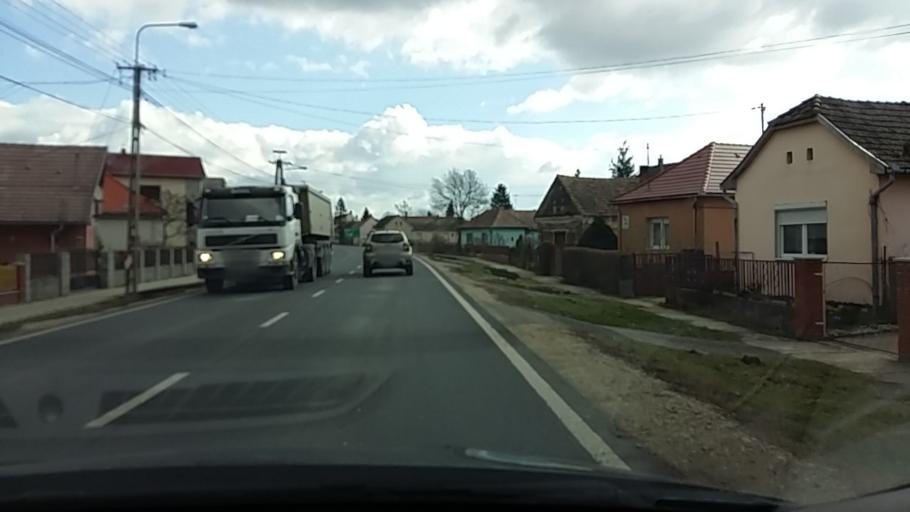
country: HU
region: Somogy
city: Nagybajom
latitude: 46.3919
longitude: 17.5053
